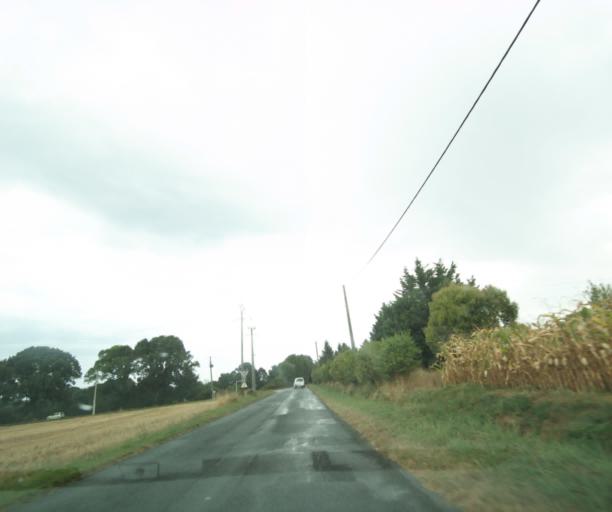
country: FR
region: Poitou-Charentes
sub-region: Departement de la Charente-Maritime
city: Tonnay-Charente
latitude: 45.9404
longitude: -0.8741
